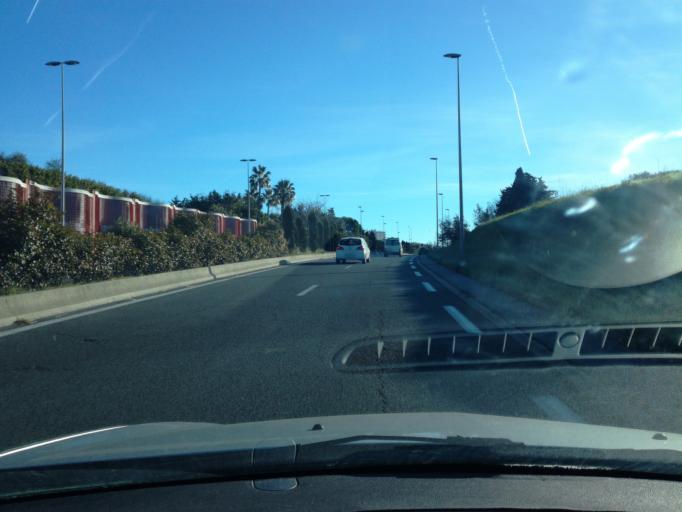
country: FR
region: Provence-Alpes-Cote d'Azur
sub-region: Departement des Alpes-Maritimes
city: Antibes
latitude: 43.5794
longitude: 7.0960
